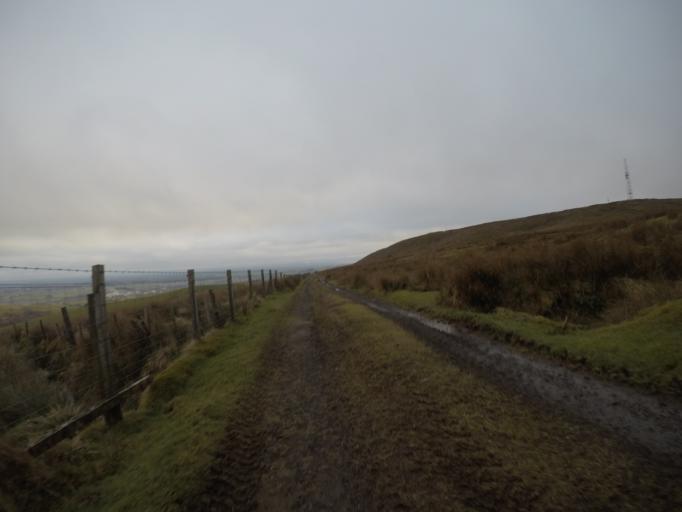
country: GB
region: Scotland
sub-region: North Ayrshire
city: Dalry
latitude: 55.7330
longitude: -4.7669
